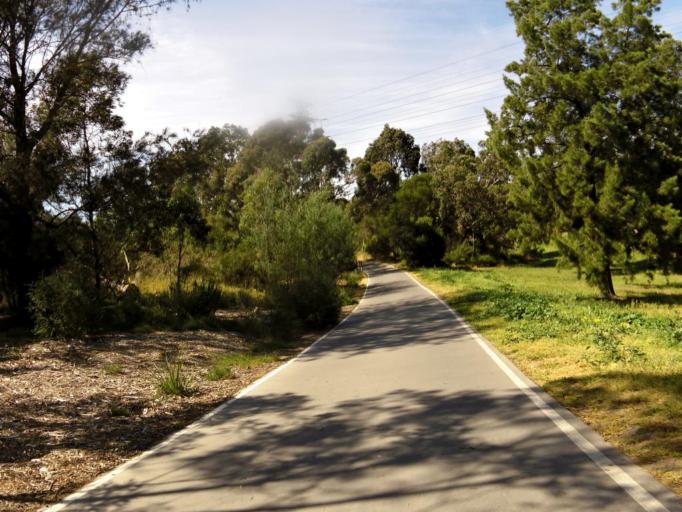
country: AU
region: Victoria
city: Albert Park
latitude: -37.8318
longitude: 145.0087
